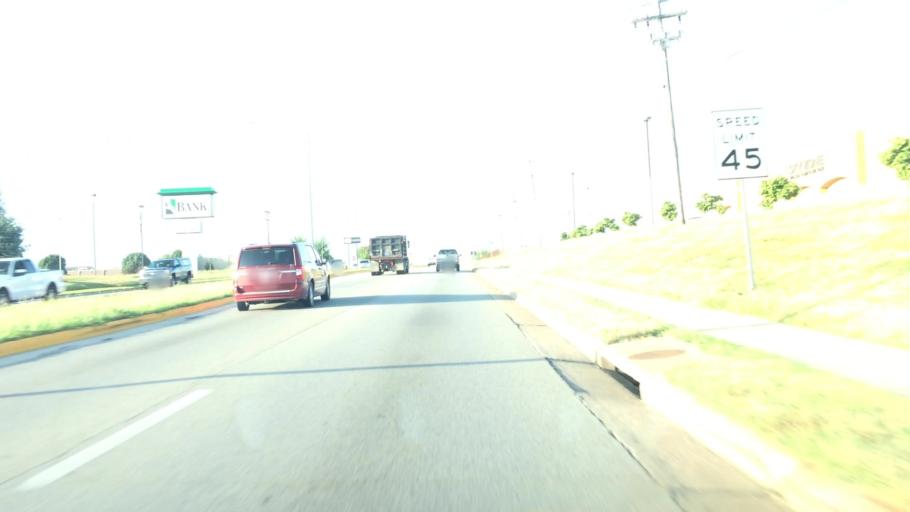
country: US
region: Missouri
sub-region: Greene County
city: Springfield
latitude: 37.1655
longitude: -93.3163
